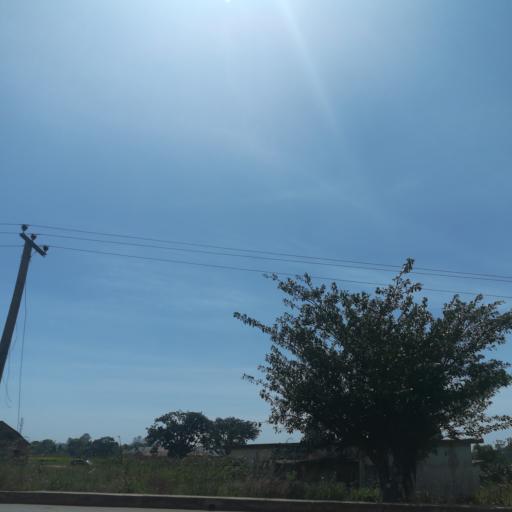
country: NG
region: Plateau
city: Bukuru
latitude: 9.7883
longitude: 8.8730
